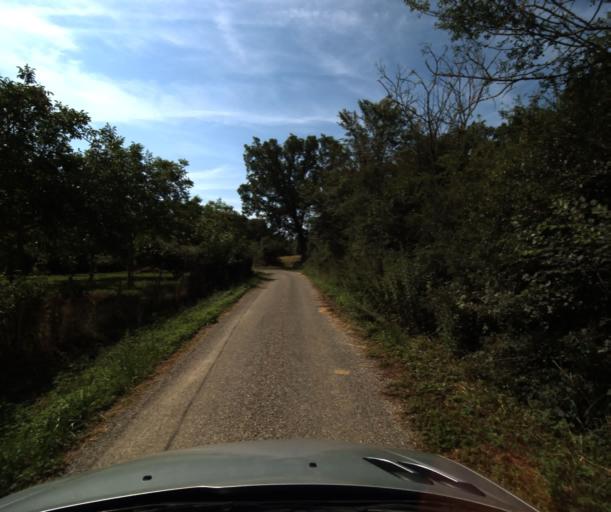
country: FR
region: Midi-Pyrenees
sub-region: Departement de la Haute-Garonne
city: Labastidette
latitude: 43.4680
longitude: 1.2210
